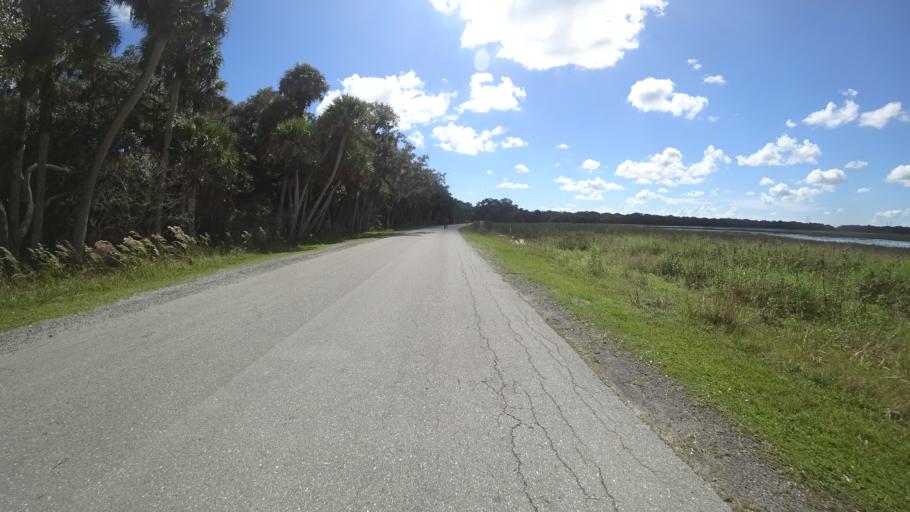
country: US
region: Florida
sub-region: Sarasota County
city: Lake Sarasota
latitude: 27.2575
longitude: -82.2878
